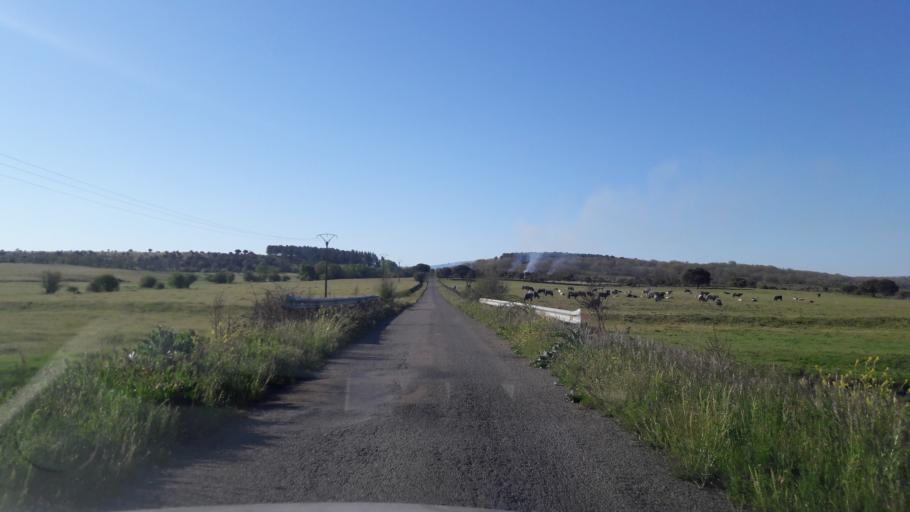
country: ES
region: Castille and Leon
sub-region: Provincia de Salamanca
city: Endrinal
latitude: 40.6108
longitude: -5.8218
